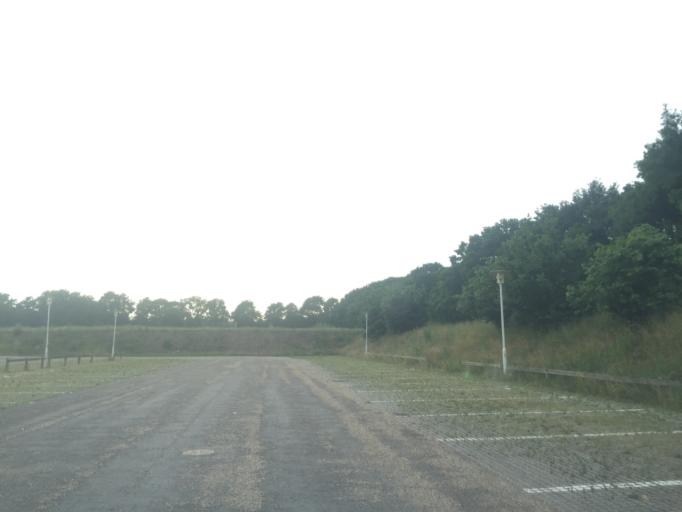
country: DK
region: Capital Region
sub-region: Lyngby-Tarbaek Kommune
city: Kongens Lyngby
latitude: 55.7802
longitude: 12.5348
